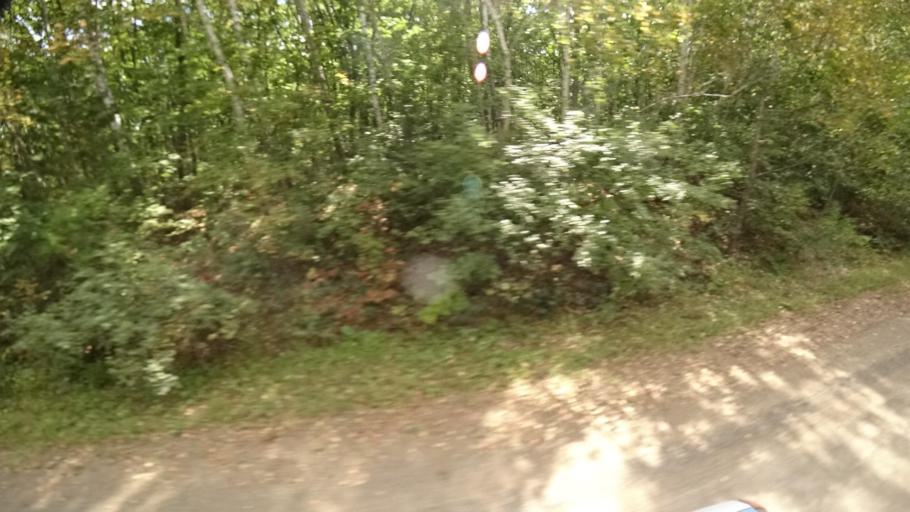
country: RU
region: Primorskiy
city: Yakovlevka
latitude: 44.7007
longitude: 133.6448
